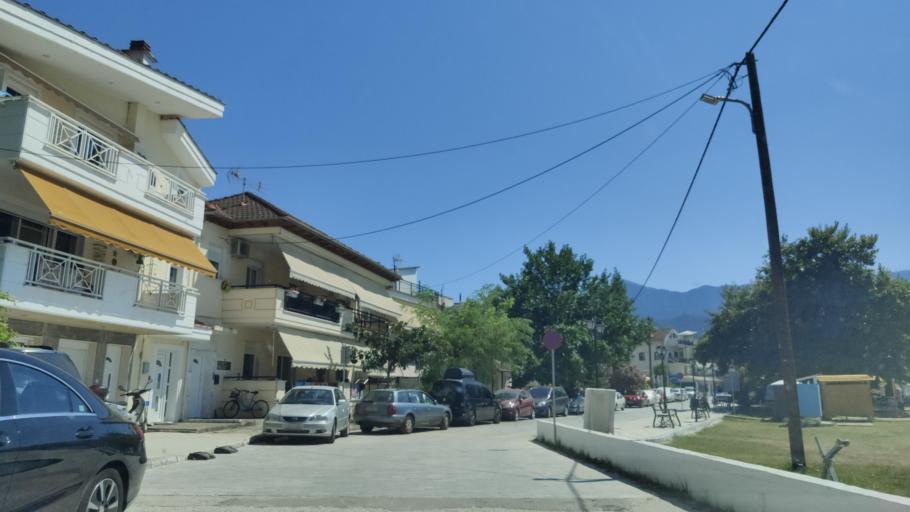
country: GR
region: East Macedonia and Thrace
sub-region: Nomos Kavalas
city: Thasos
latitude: 40.7836
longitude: 24.7153
